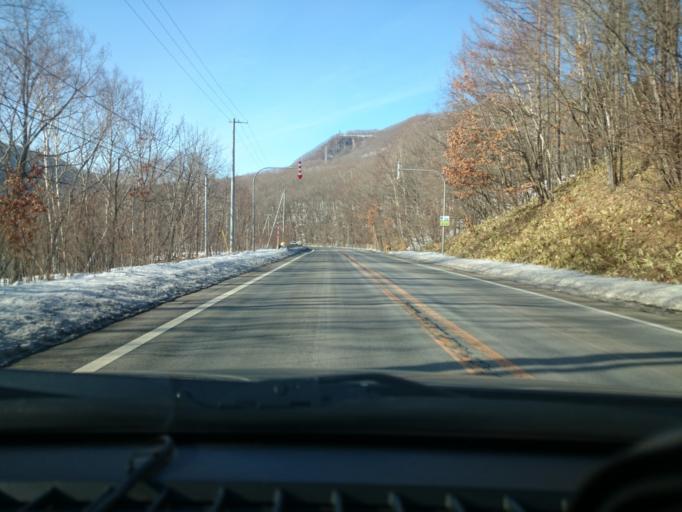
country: JP
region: Hokkaido
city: Otofuke
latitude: 43.2531
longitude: 143.4720
